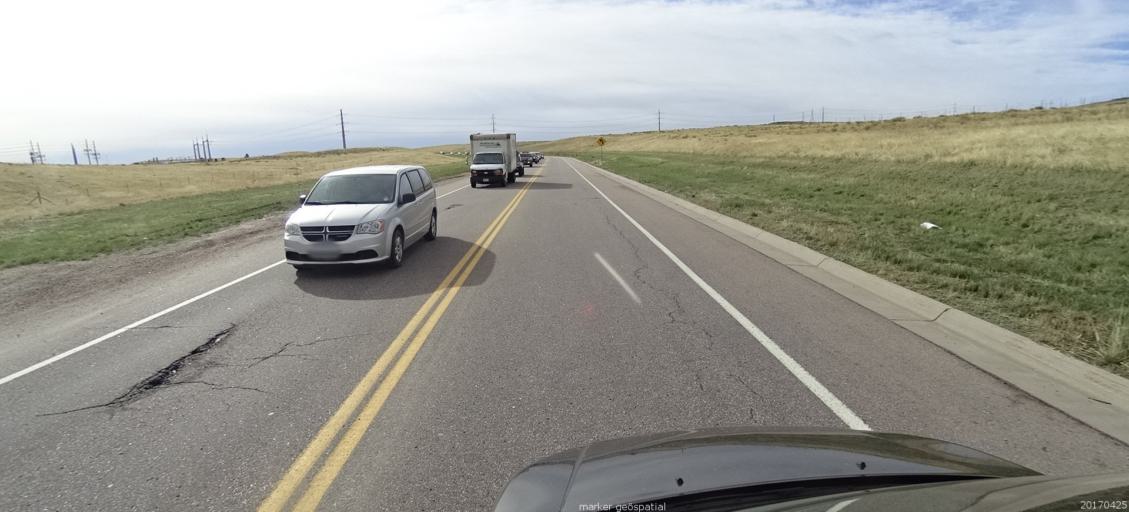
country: US
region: Colorado
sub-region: Douglas County
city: Meridian
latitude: 39.5216
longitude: -104.8523
